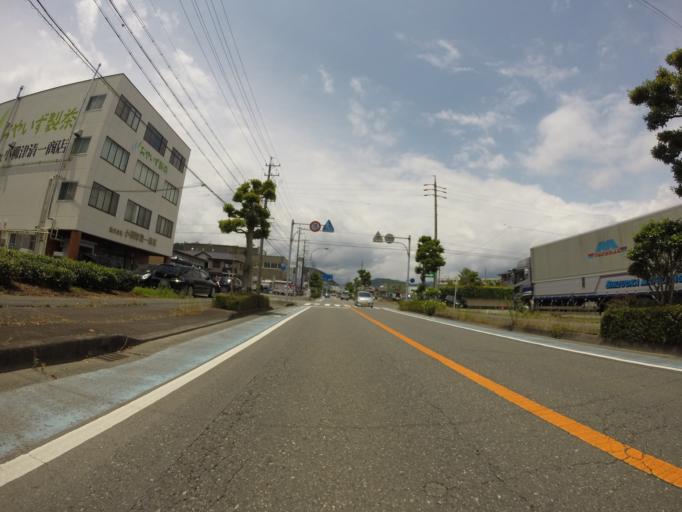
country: JP
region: Shizuoka
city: Shizuoka-shi
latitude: 34.9692
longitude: 138.3522
